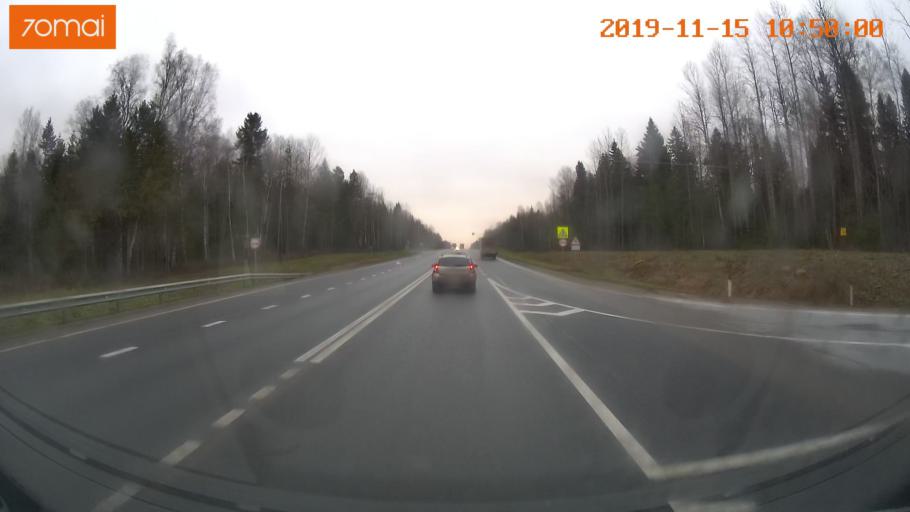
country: RU
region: Vologda
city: Sheksna
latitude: 59.1875
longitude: 38.6717
